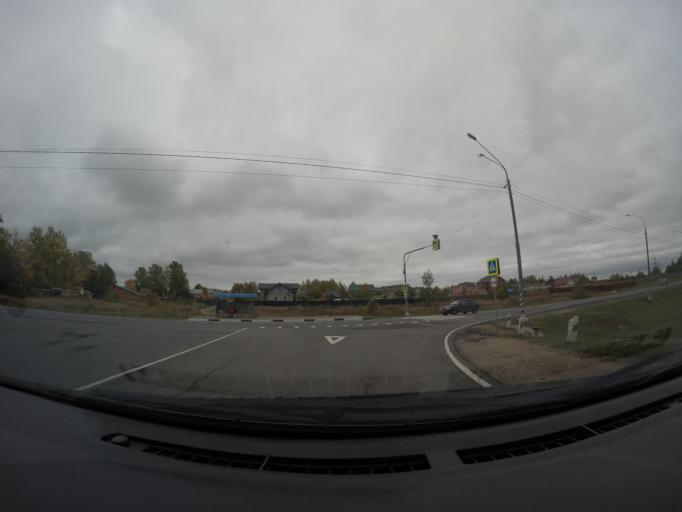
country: RU
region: Moskovskaya
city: Ruza
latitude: 55.7730
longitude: 36.2657
